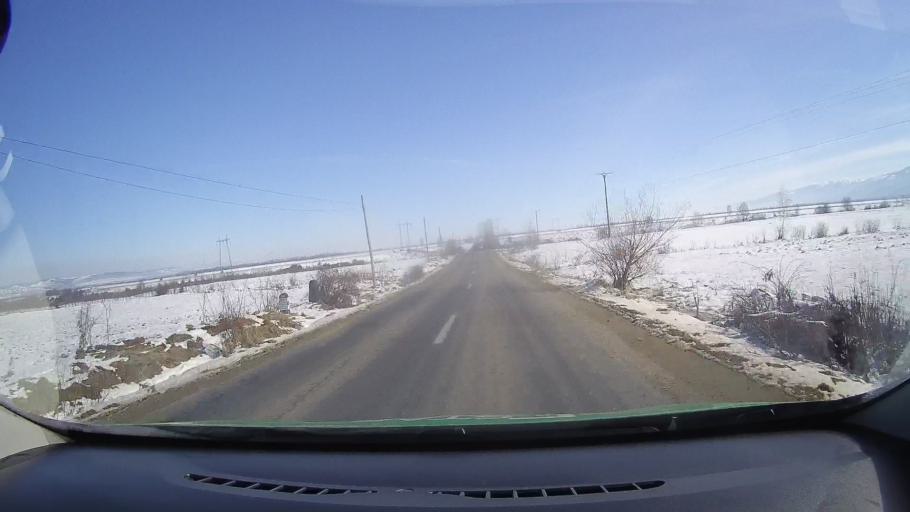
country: RO
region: Brasov
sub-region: Oras Victoria
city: Victoria
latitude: 45.7318
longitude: 24.7191
